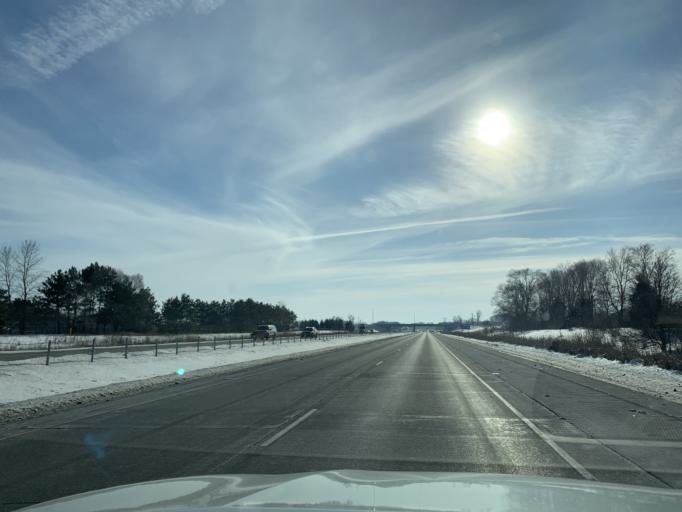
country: US
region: Minnesota
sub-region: Washington County
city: Forest Lake
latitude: 45.2946
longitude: -93.0030
